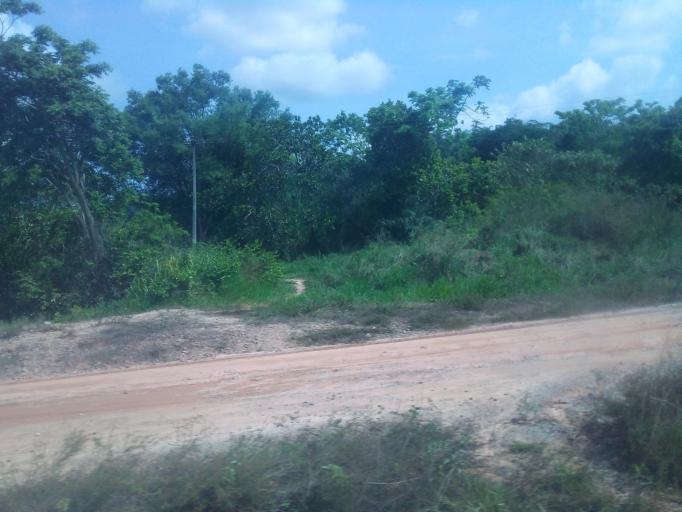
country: BR
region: Maranhao
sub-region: Santa Ines
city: Santa Ines
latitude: -3.9480
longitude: -46.2267
